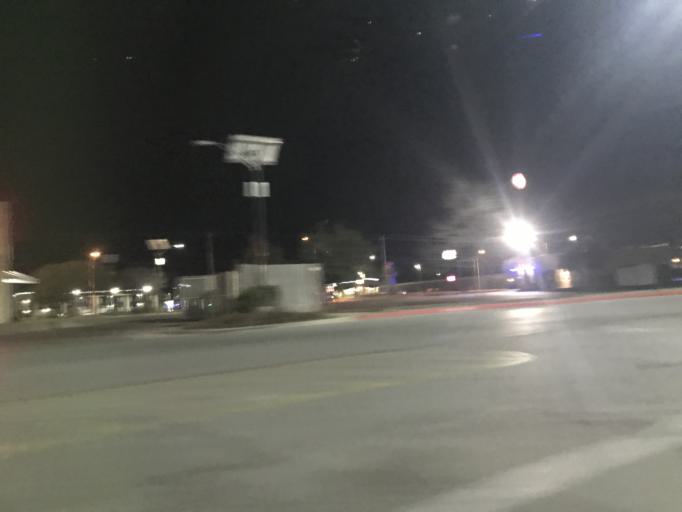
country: US
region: Texas
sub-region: Taylor County
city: Abilene
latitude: 32.4792
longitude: -99.6980
